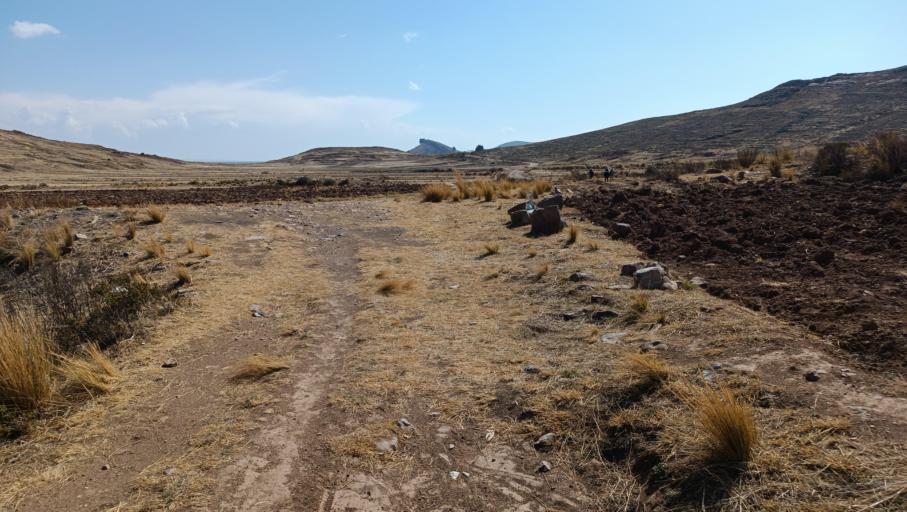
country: BO
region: La Paz
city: Batallas
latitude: -16.3484
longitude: -68.6659
